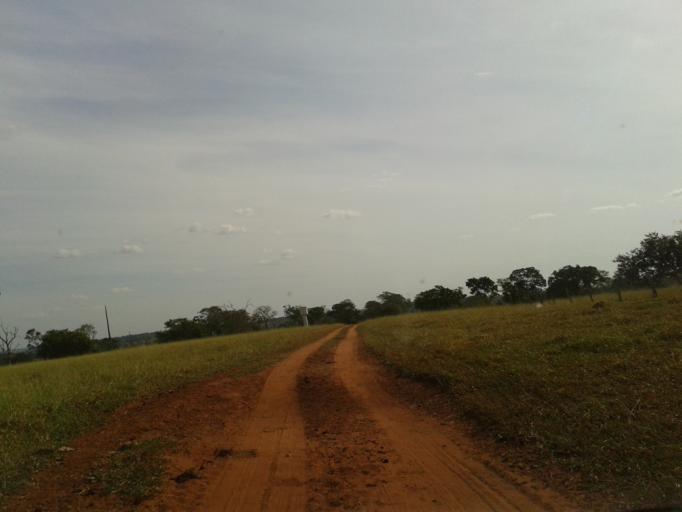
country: BR
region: Minas Gerais
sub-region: Campina Verde
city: Campina Verde
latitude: -19.5144
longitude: -49.5908
